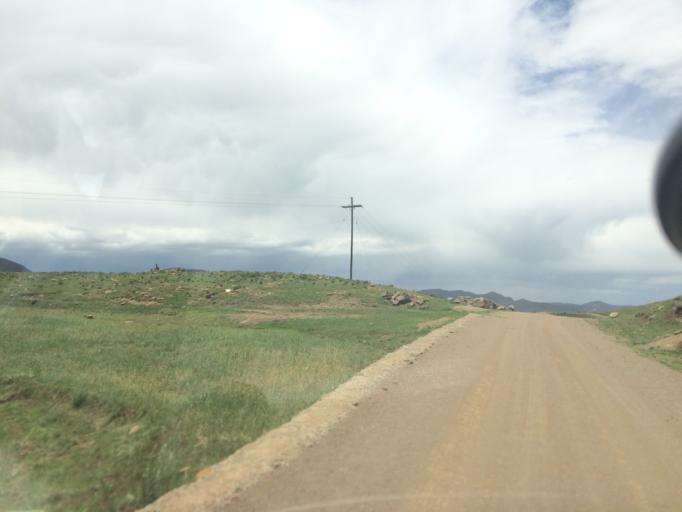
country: LS
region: Maseru
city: Nako
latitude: -29.8688
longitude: 28.0398
